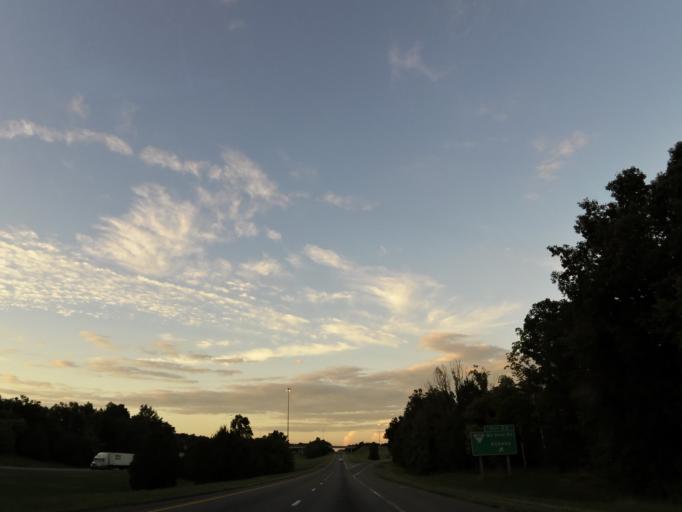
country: US
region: Tennessee
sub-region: McMinn County
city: Athens
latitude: 35.4997
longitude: -84.6145
